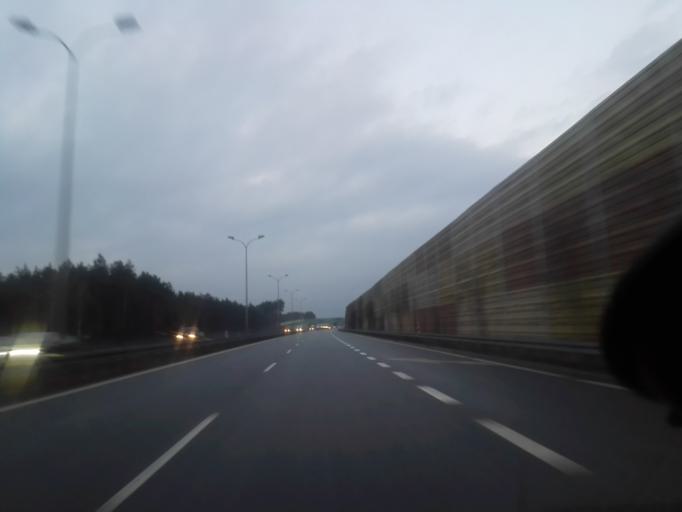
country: PL
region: Masovian Voivodeship
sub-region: Powiat wolominski
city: Tluszcz
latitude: 52.5124
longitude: 21.3964
